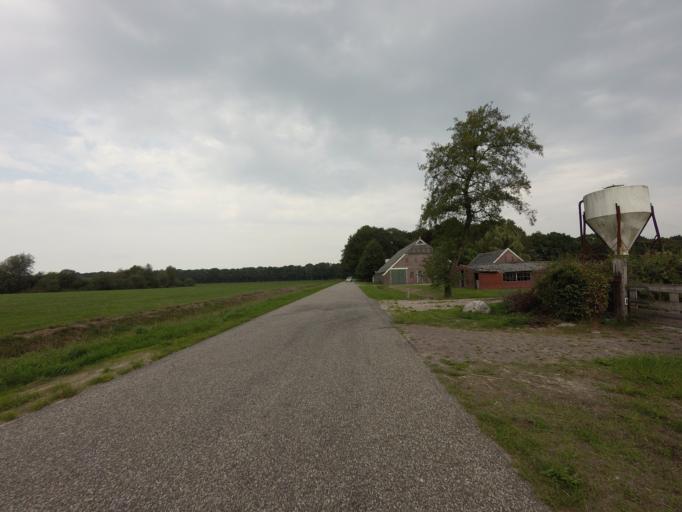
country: NL
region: Drenthe
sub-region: Gemeente Tynaarlo
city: Vries
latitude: 53.0566
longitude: 6.5879
